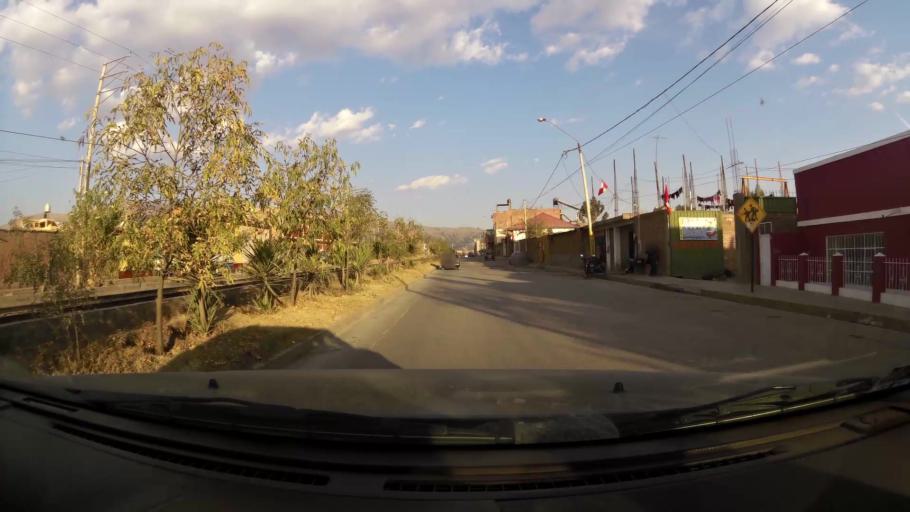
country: PE
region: Junin
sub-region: Provincia de Huancayo
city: El Tambo
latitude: -12.0423
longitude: -75.2213
